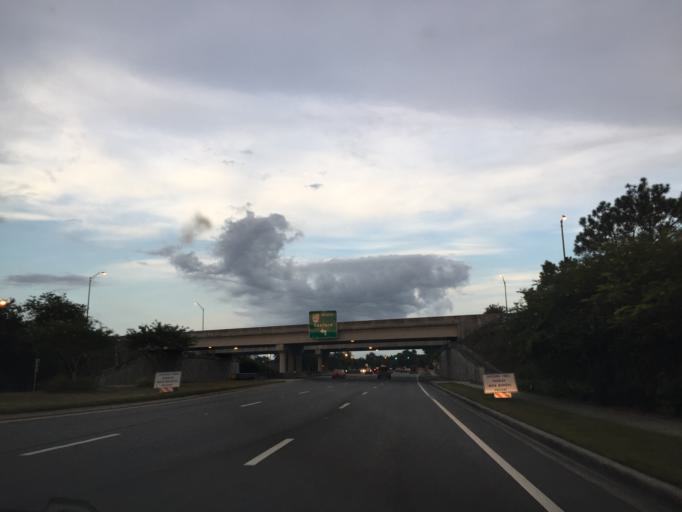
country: US
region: Florida
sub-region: Seminole County
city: Oviedo
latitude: 28.6563
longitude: -81.2335
